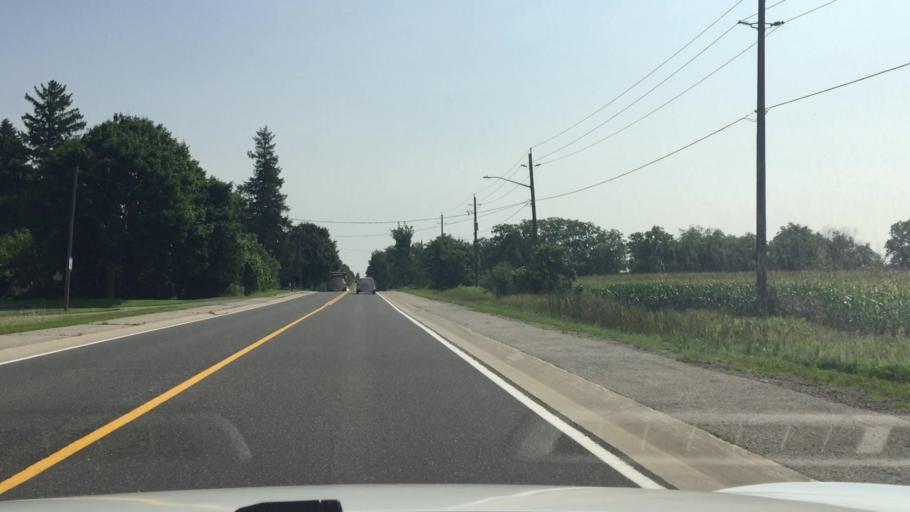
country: CA
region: Ontario
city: Pickering
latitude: 43.9020
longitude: -79.1801
